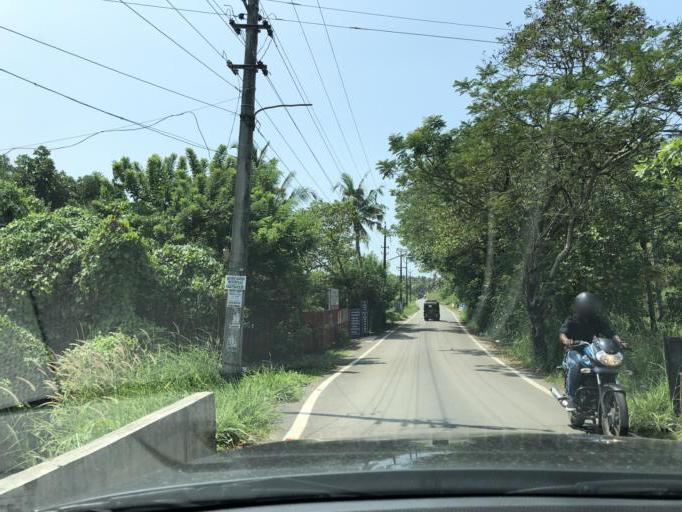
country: IN
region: Kerala
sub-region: Ernakulam
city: Cochin
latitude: 9.9903
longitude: 76.2318
